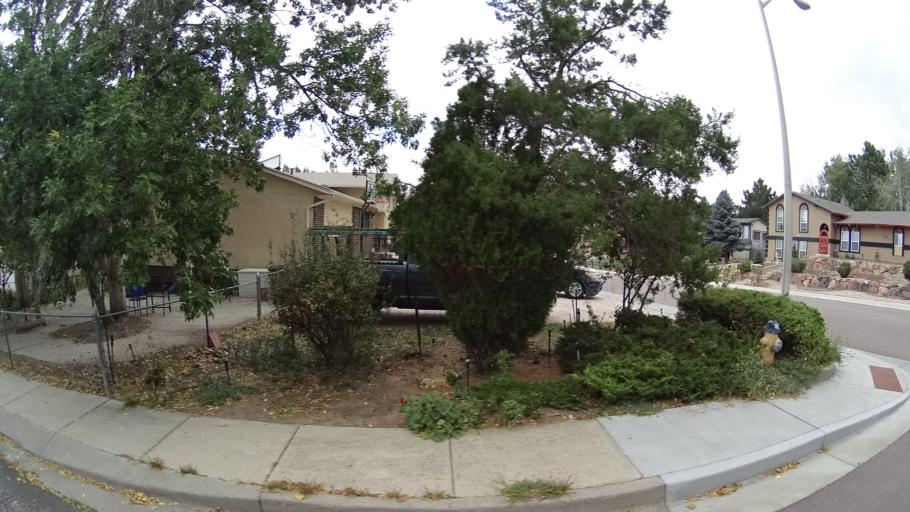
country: US
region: Colorado
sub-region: El Paso County
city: Cimarron Hills
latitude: 38.8934
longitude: -104.7343
